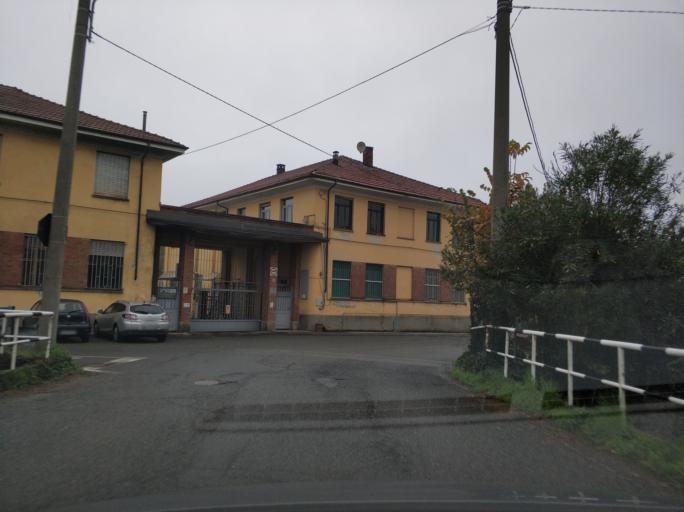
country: IT
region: Piedmont
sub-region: Provincia di Torino
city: Cirie
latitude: 45.2244
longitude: 7.5825
